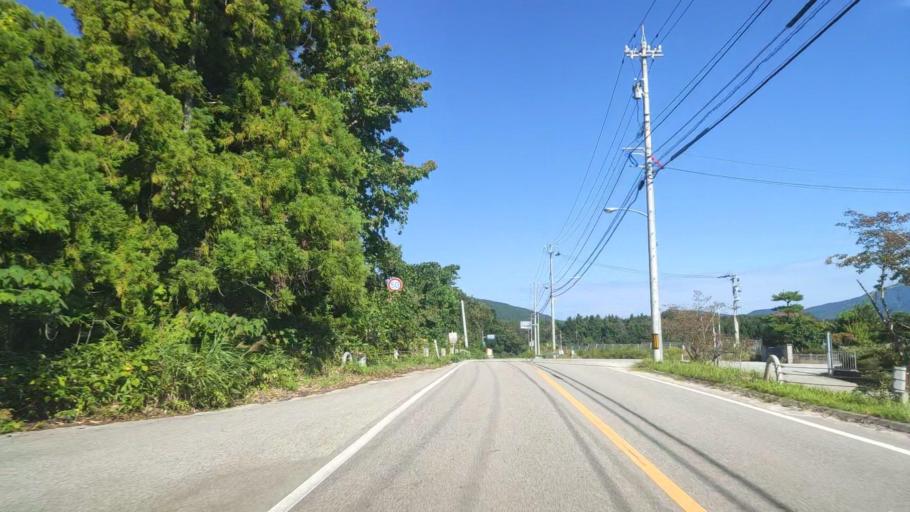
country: JP
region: Ishikawa
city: Nanao
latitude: 37.1731
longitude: 136.7138
